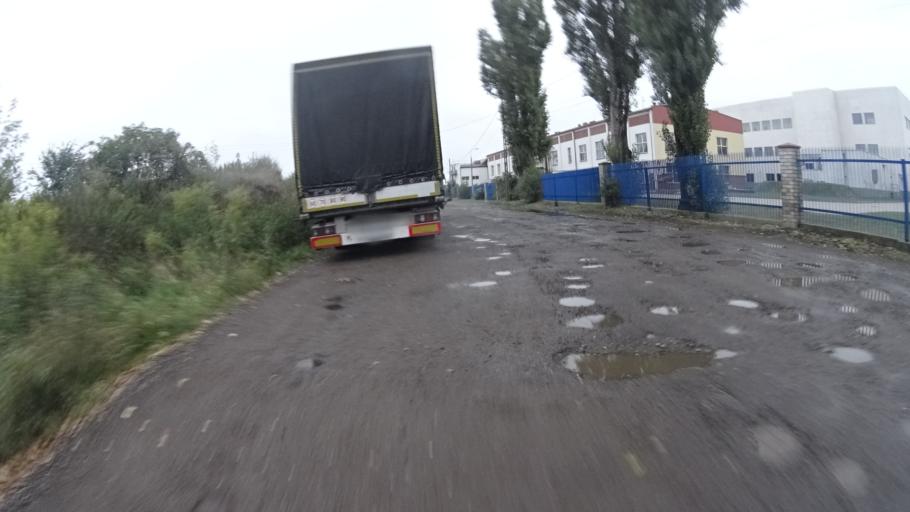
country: PL
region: Masovian Voivodeship
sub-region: Powiat warszawski zachodni
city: Babice
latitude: 52.2248
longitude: 20.8644
